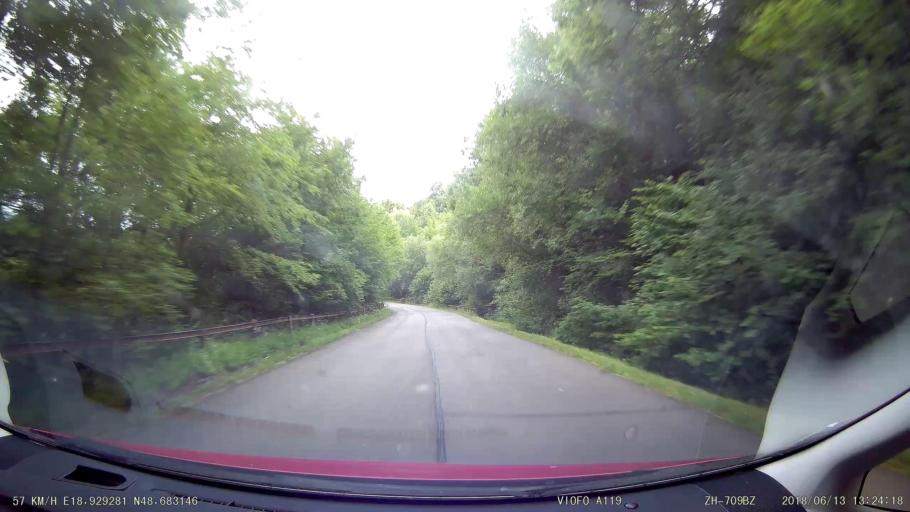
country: SK
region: Banskobystricky
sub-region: Okres Ziar nad Hronom
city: Kremnica
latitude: 48.6832
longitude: 18.9293
